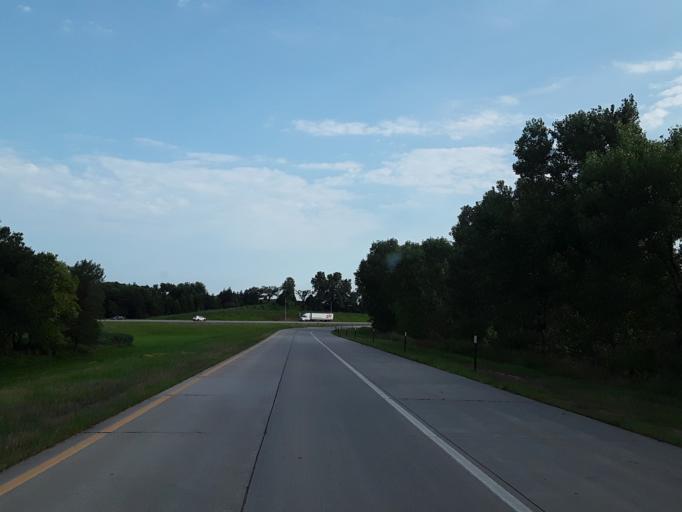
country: US
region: Nebraska
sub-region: Saunders County
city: Ashland
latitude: 41.0118
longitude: -96.3102
